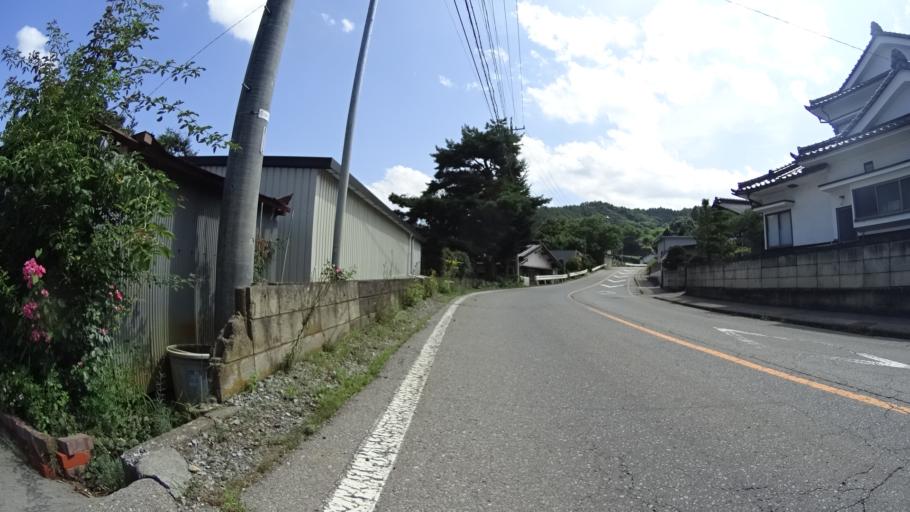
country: JP
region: Nagano
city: Saku
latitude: 36.0599
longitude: 138.4655
